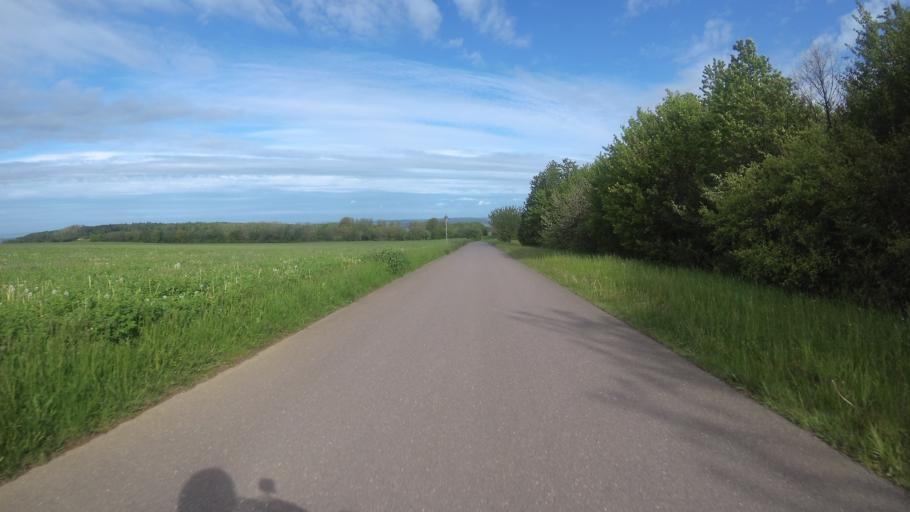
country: DE
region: Saarland
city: Perl
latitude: 49.4780
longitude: 6.4250
